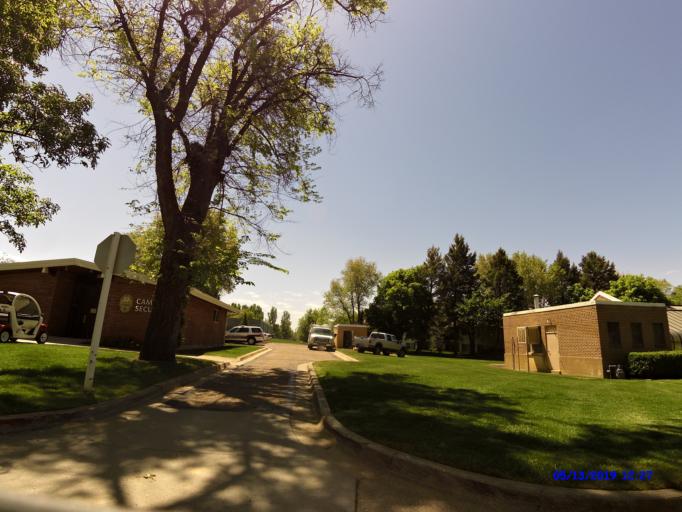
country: US
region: Utah
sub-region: Weber County
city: Harrisville
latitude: 41.2630
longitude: -111.9669
